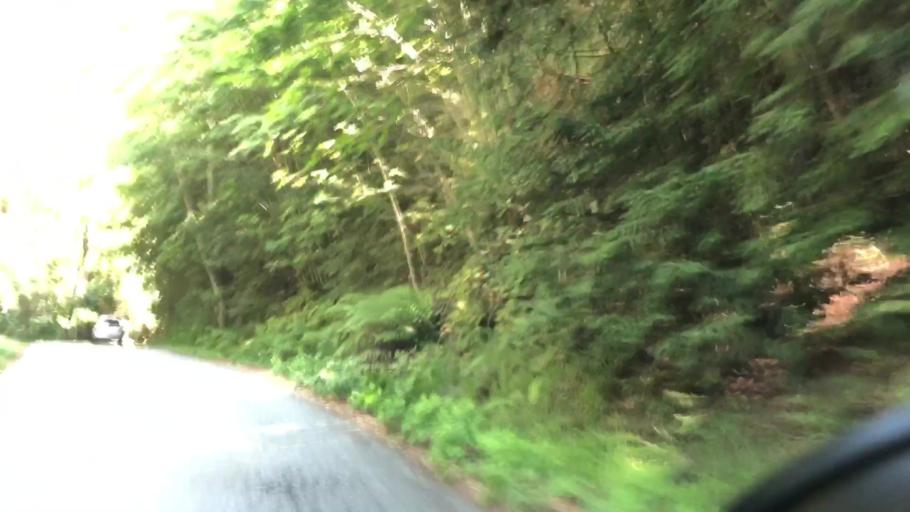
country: US
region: California
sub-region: Santa Cruz County
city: Day Valley
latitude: 37.0286
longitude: -121.8211
